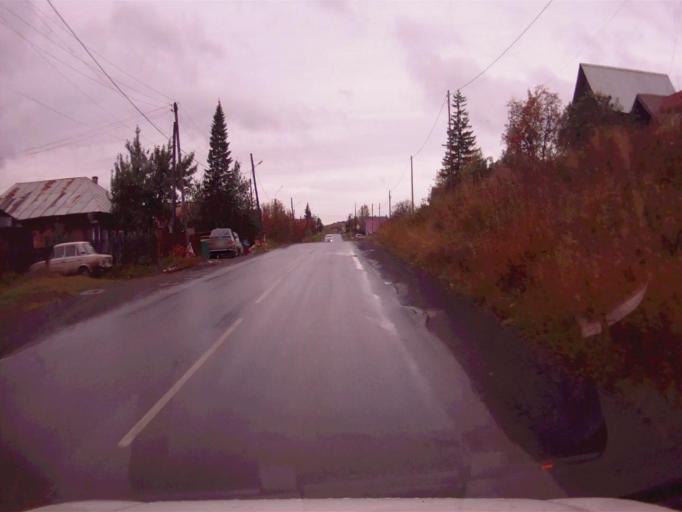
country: RU
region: Chelyabinsk
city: Verkhniy Ufaley
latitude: 56.0530
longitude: 60.2044
